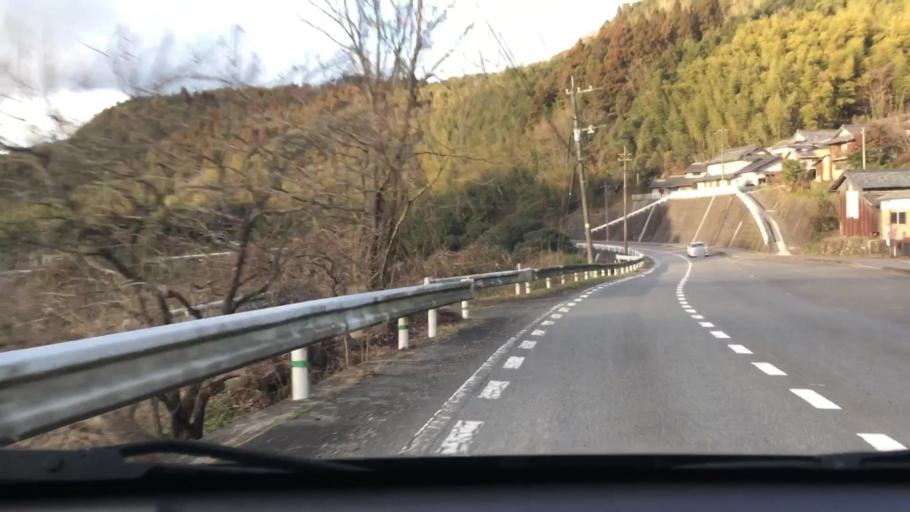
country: JP
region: Oita
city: Hiji
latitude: 33.4187
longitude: 131.4191
